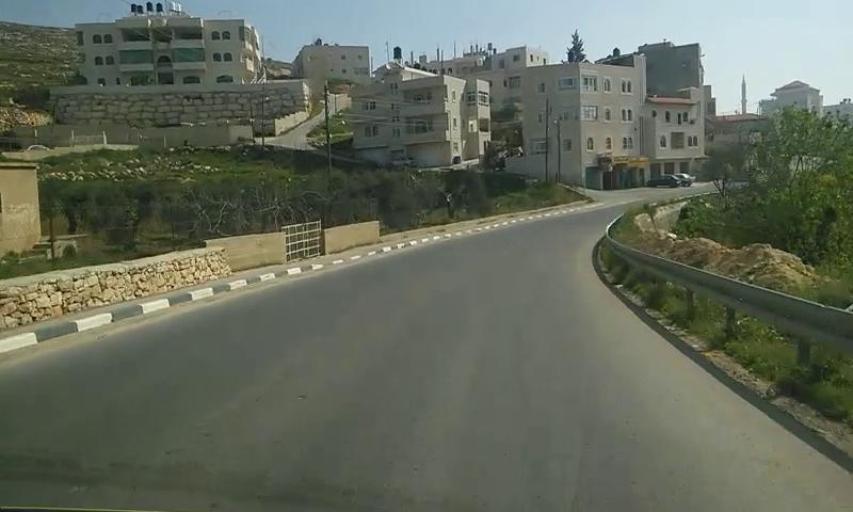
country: PS
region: West Bank
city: Dayr Jarir
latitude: 31.9709
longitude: 35.2845
